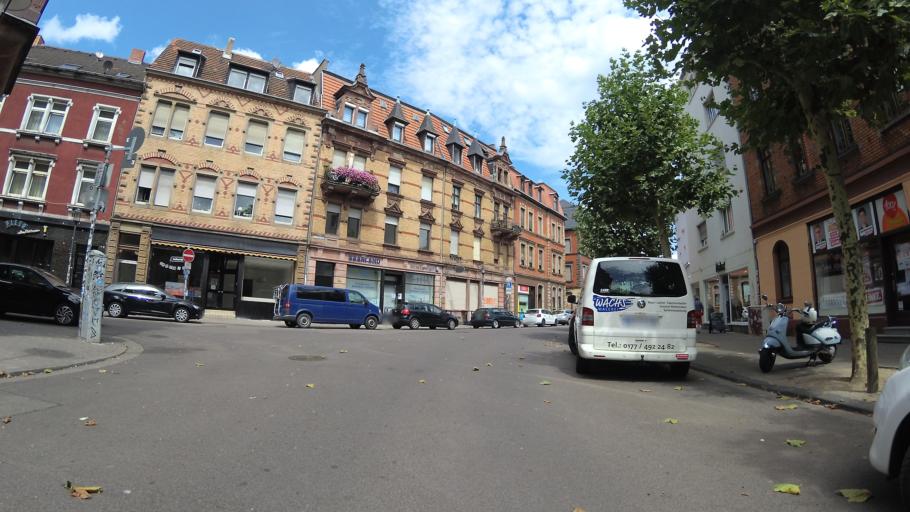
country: DE
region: Saarland
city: Saarbrucken
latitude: 49.2359
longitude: 6.9998
